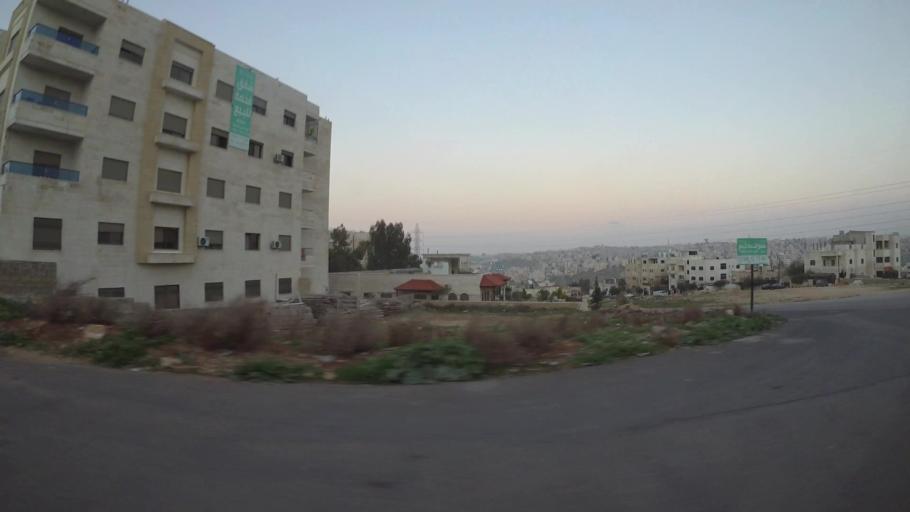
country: JO
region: Amman
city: Amman
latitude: 31.9896
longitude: 35.9716
